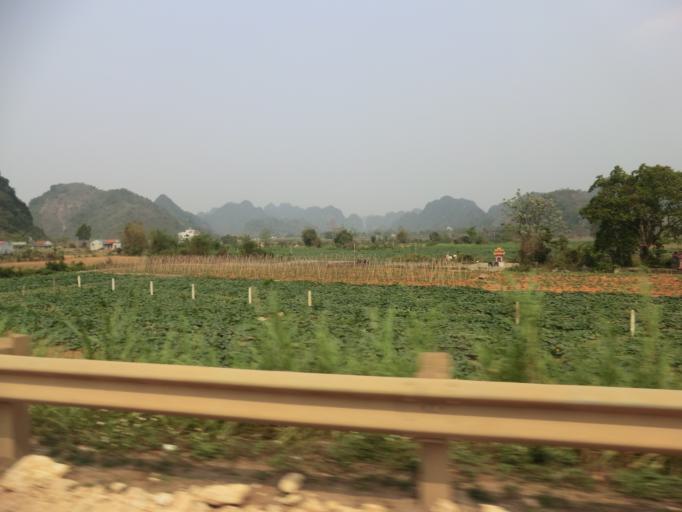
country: VN
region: Hoa Binh
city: Thi Tran Hang Tram
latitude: 20.4478
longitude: 105.6305
